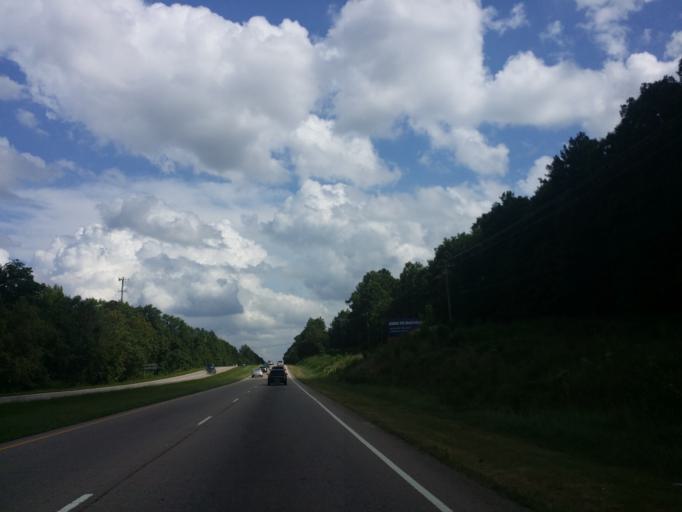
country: US
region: North Carolina
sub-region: Wake County
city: Morrisville
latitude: 35.9295
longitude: -78.8058
